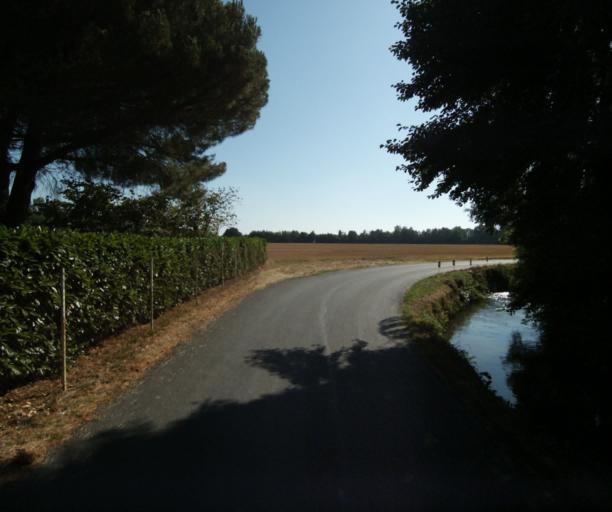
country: FR
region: Midi-Pyrenees
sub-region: Departement de la Haute-Garonne
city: Revel
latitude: 43.4750
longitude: 1.9929
